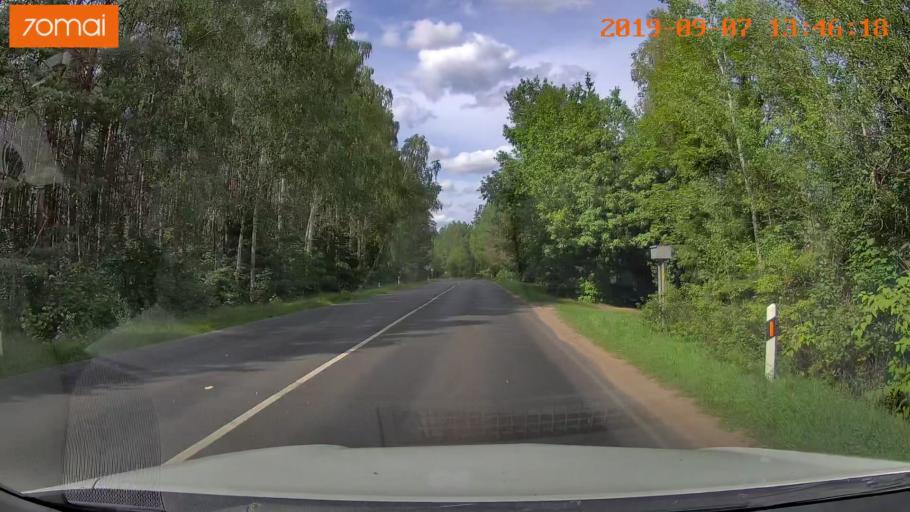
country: LT
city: Baltoji Voke
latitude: 54.5902
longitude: 25.2342
